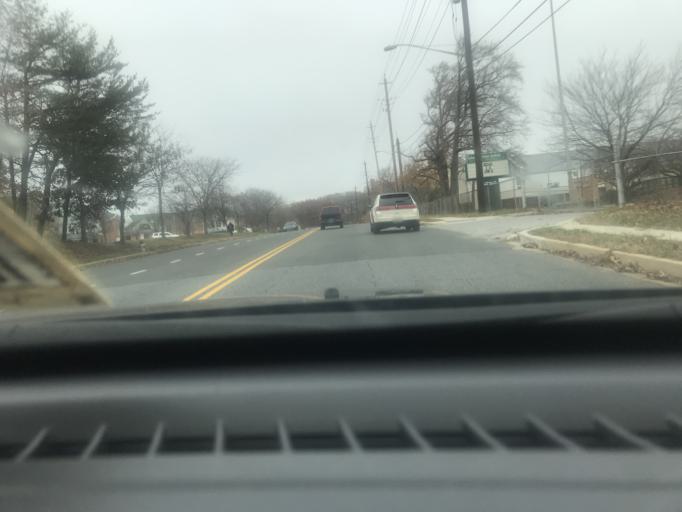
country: US
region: Maryland
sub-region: Prince George's County
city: Oxon Hill
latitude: 38.7978
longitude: -76.9779
